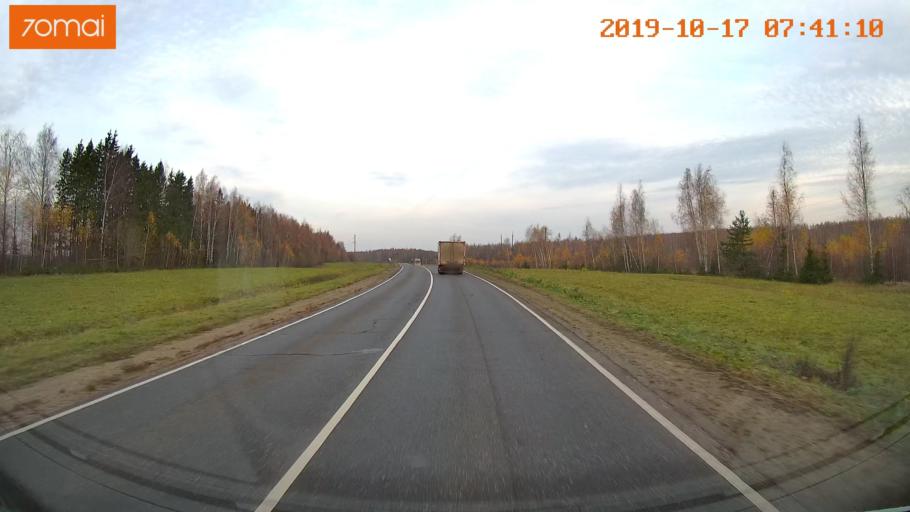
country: RU
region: Vladimir
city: Yur'yev-Pol'skiy
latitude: 56.4799
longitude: 39.8158
